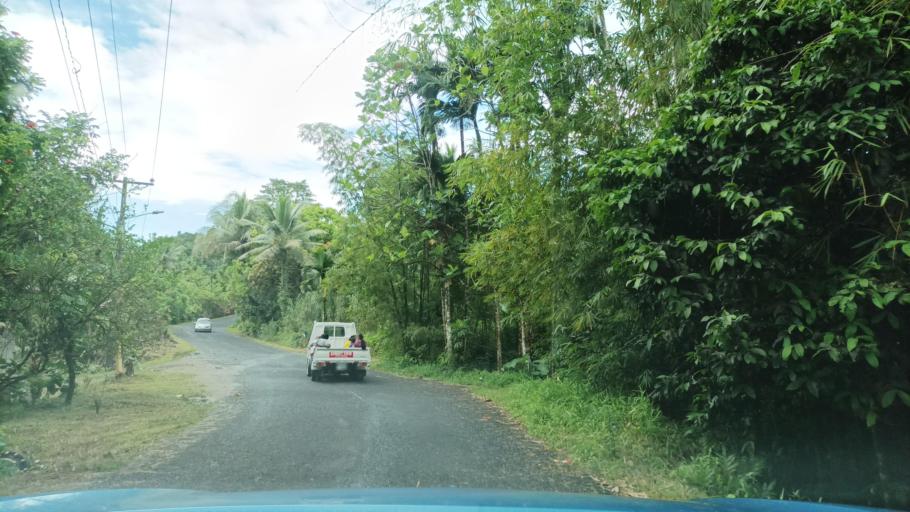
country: FM
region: Pohnpei
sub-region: Sokehs Municipality
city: Palikir - National Government Center
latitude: 6.8529
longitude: 158.1623
